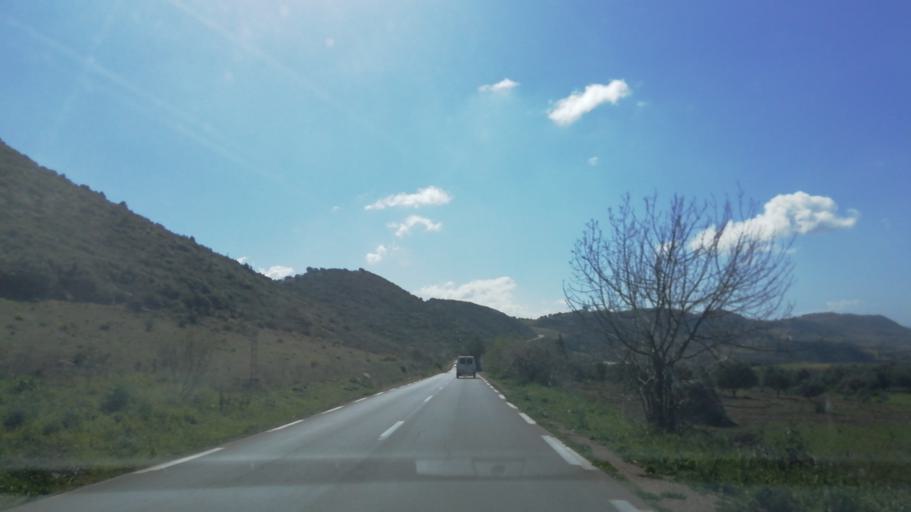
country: DZ
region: Mascara
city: Mascara
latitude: 35.4709
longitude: 0.1550
